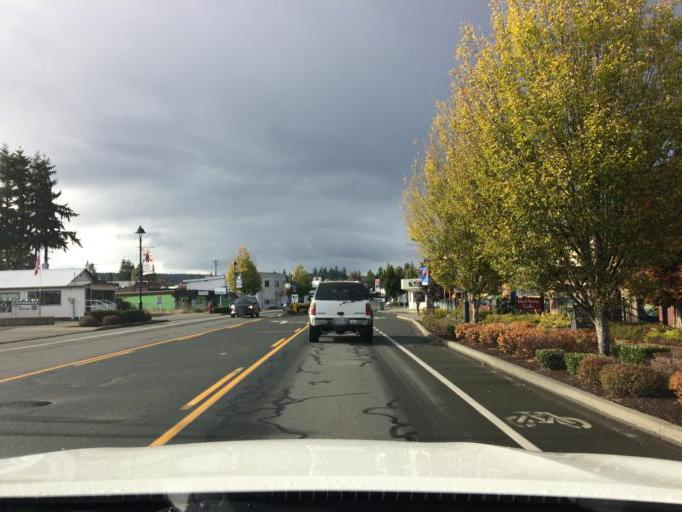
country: CA
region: British Columbia
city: Campbell River
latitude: 49.9707
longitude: -125.2151
